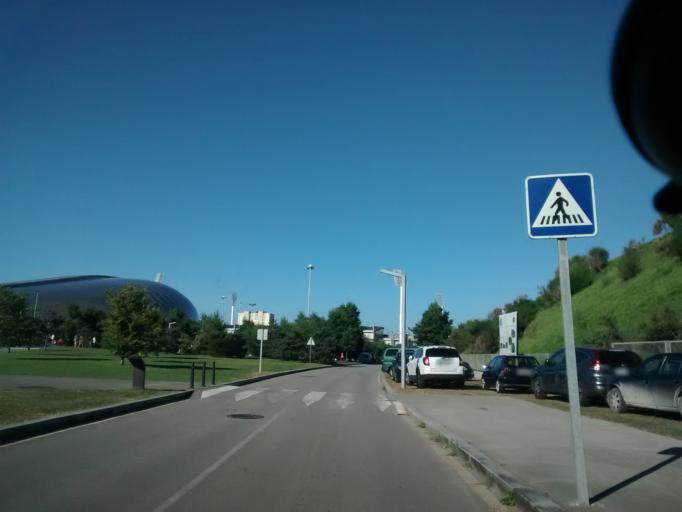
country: ES
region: Cantabria
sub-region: Provincia de Cantabria
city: Santander
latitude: 43.4737
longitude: -3.7970
